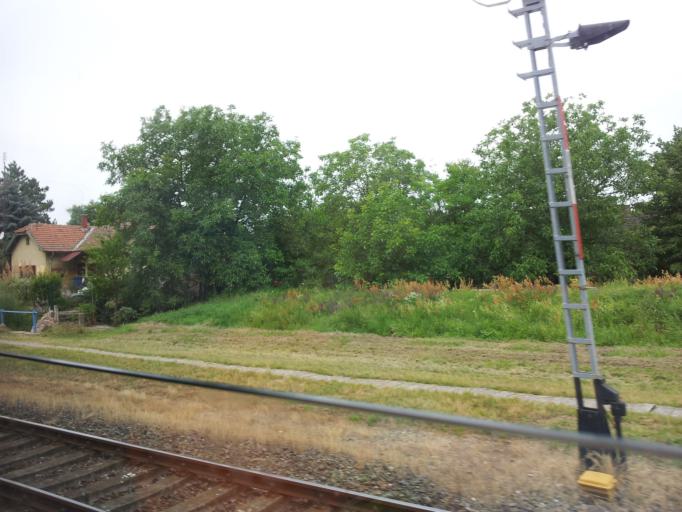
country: HU
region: Veszprem
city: Zanka
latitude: 46.8798
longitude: 17.7433
